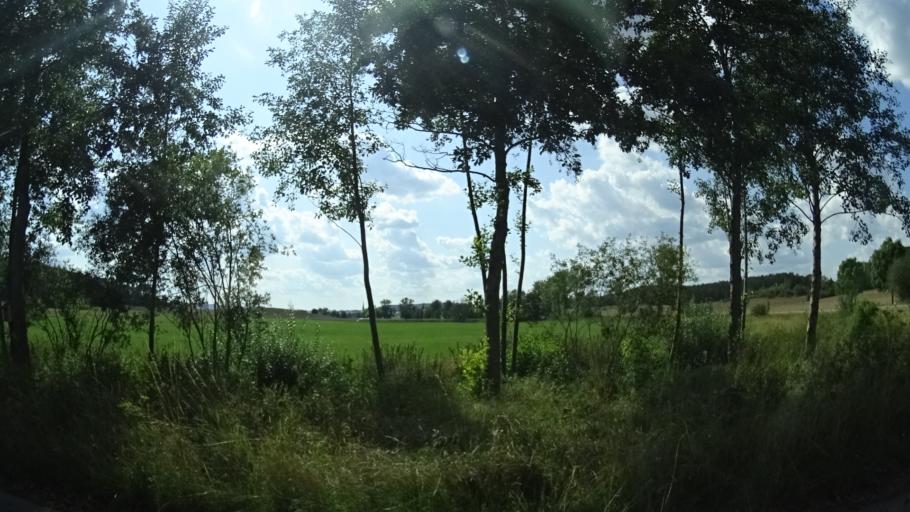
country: DE
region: Bavaria
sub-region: Regierungsbezirk Unterfranken
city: Trappstadt
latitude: 50.2984
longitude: 10.5848
